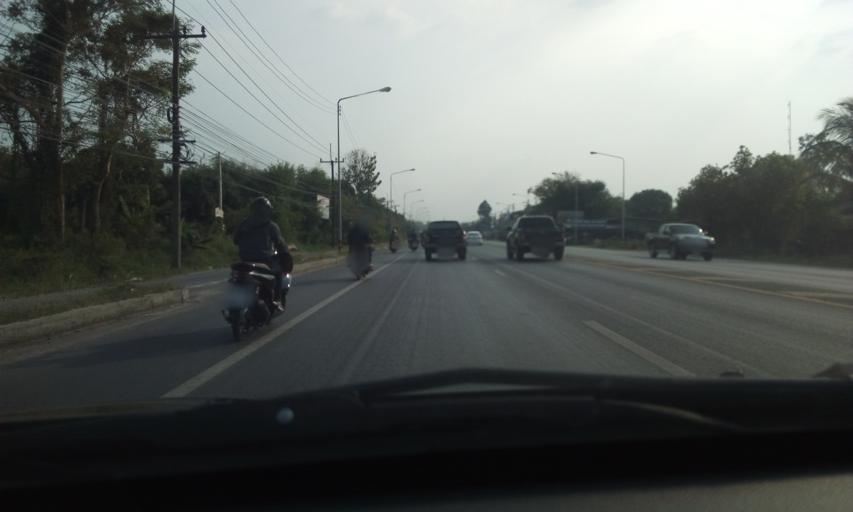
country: TH
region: Nakhon Nayok
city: Nakhon Nayok
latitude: 14.2722
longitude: 101.2737
